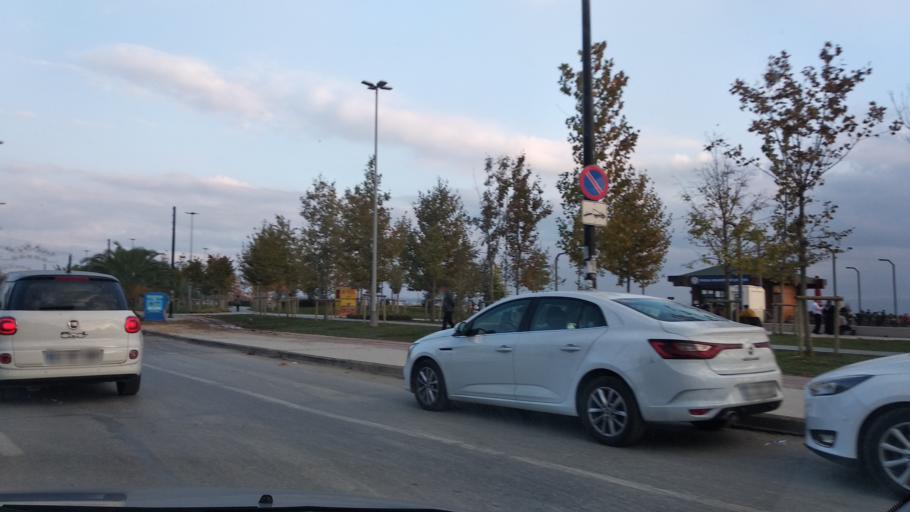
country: TR
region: Istanbul
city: Icmeler
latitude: 40.8167
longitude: 29.2977
